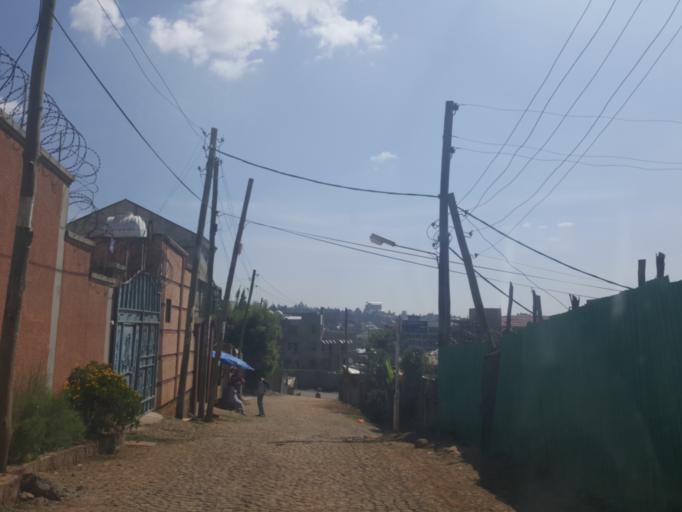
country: ET
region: Adis Abeba
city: Addis Ababa
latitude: 9.0705
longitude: 38.7165
